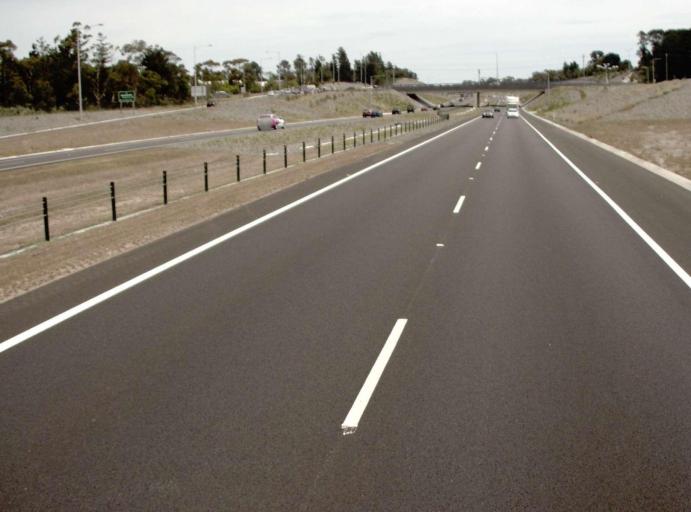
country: AU
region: Victoria
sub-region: Frankston
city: Langwarrin
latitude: -38.1527
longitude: 145.1699
